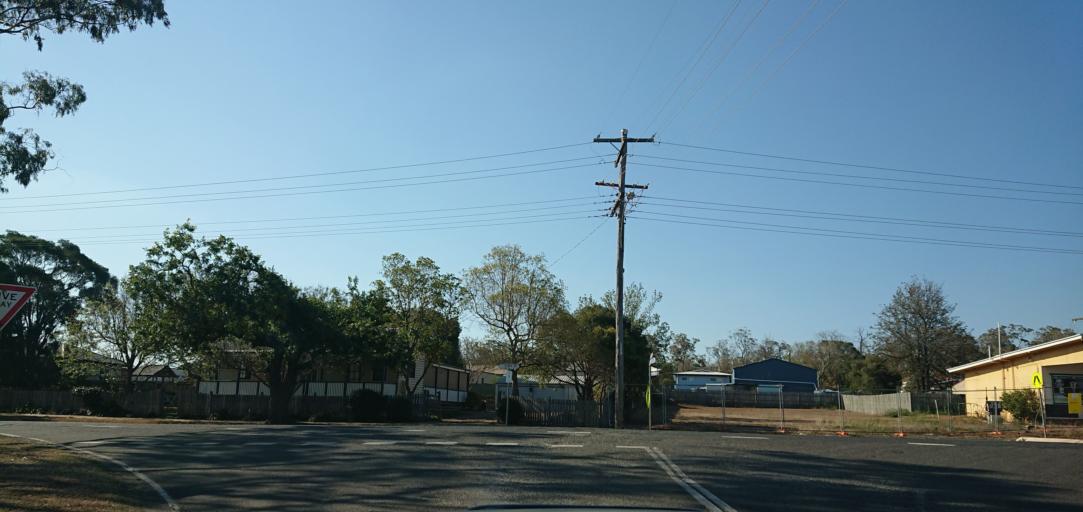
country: AU
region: Queensland
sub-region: Toowoomba
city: Westbrook
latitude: -27.6787
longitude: 151.7129
